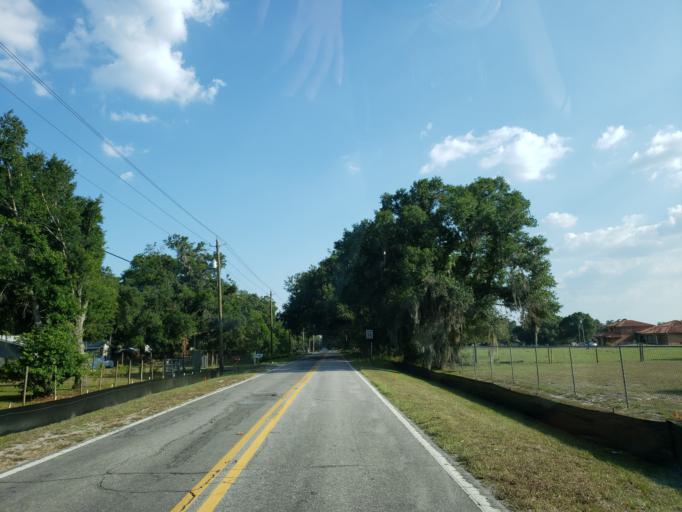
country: US
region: Florida
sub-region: Hillsborough County
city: Fish Hawk
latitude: 27.8479
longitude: -82.2000
